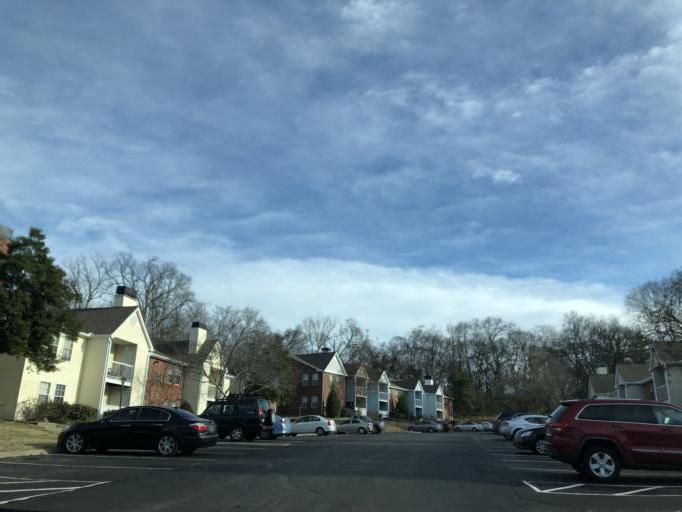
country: US
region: Tennessee
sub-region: Davidson County
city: Lakewood
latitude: 36.1480
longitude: -86.6225
